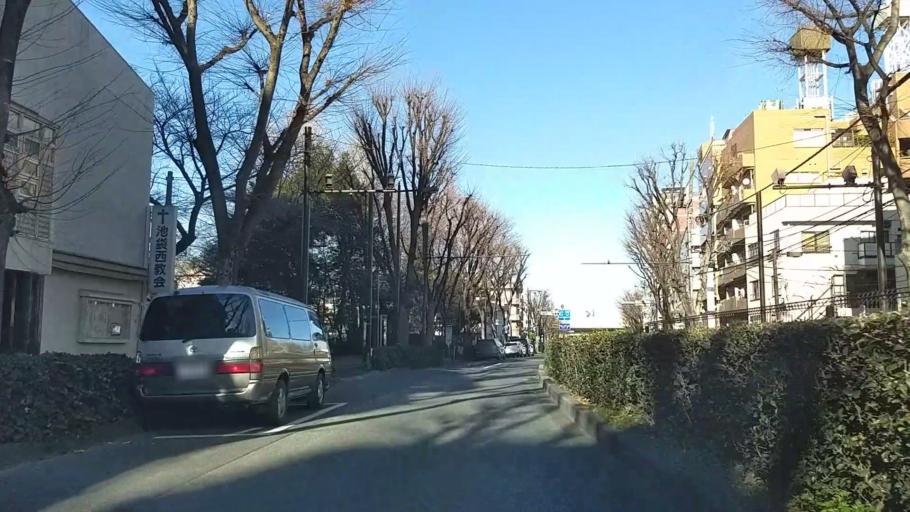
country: JP
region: Tokyo
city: Tokyo
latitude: 35.7366
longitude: 139.7097
